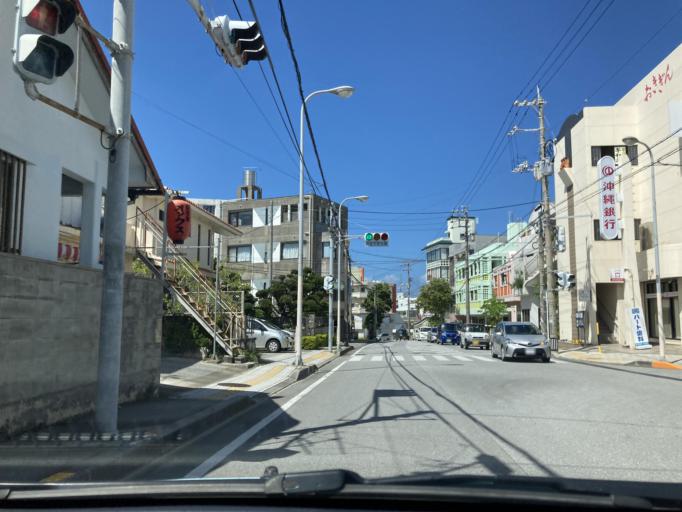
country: JP
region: Okinawa
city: Tomigusuku
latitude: 26.1935
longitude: 127.6660
